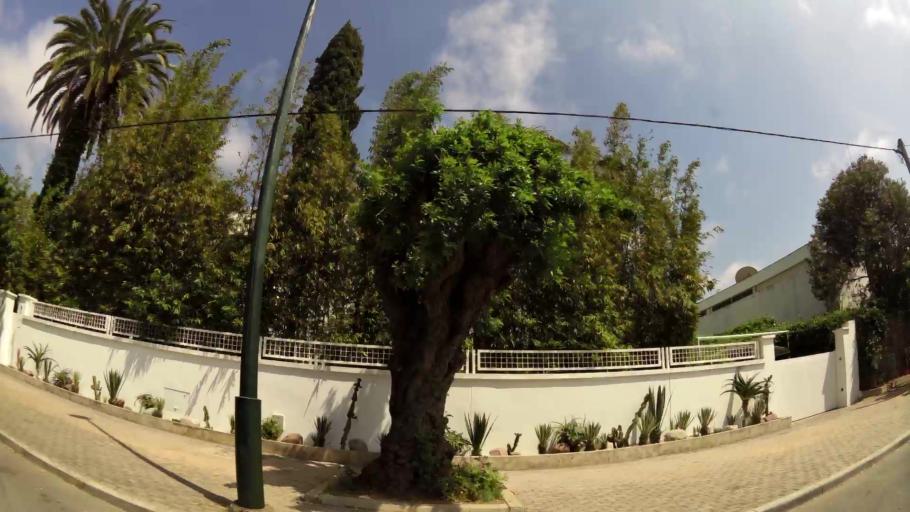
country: MA
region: Rabat-Sale-Zemmour-Zaer
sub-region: Rabat
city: Rabat
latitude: 33.9912
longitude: -6.8445
